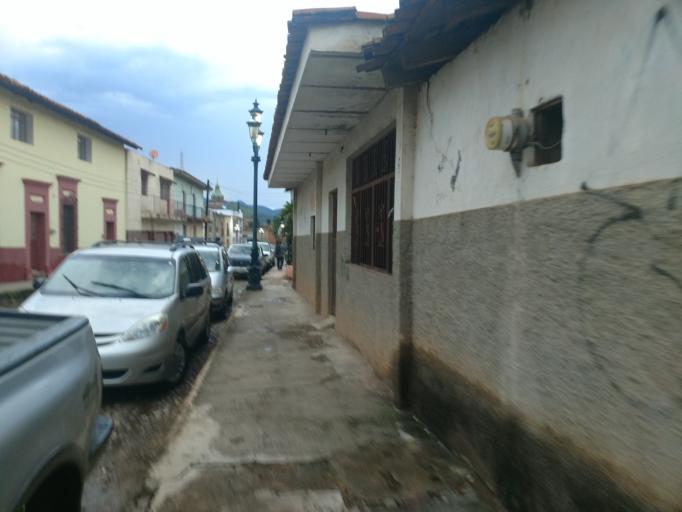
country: MX
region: Jalisco
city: Talpa de Allende
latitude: 20.3790
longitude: -104.8209
